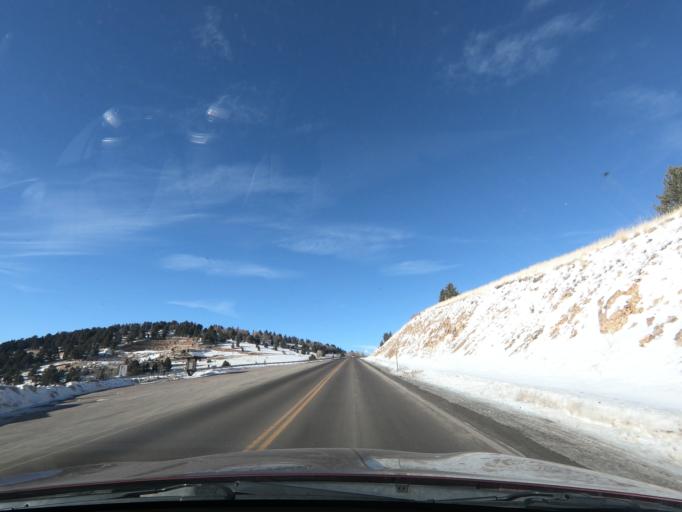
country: US
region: Colorado
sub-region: Teller County
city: Cripple Creek
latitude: 38.7588
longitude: -105.1618
